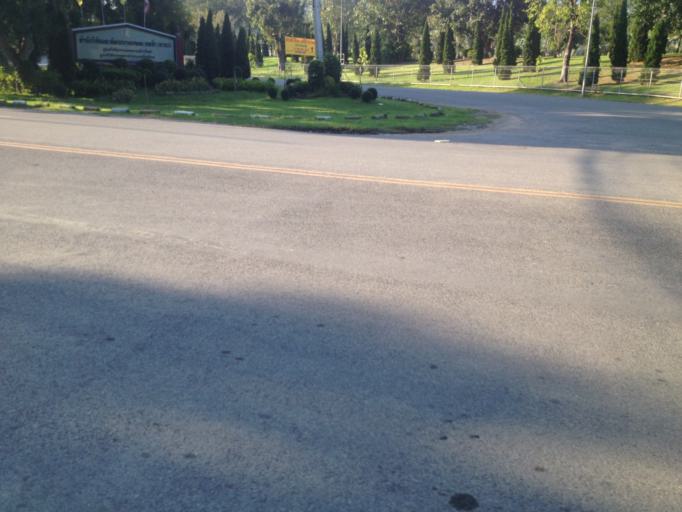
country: TH
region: Chiang Mai
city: Hang Dong
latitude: 18.7439
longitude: 98.9252
